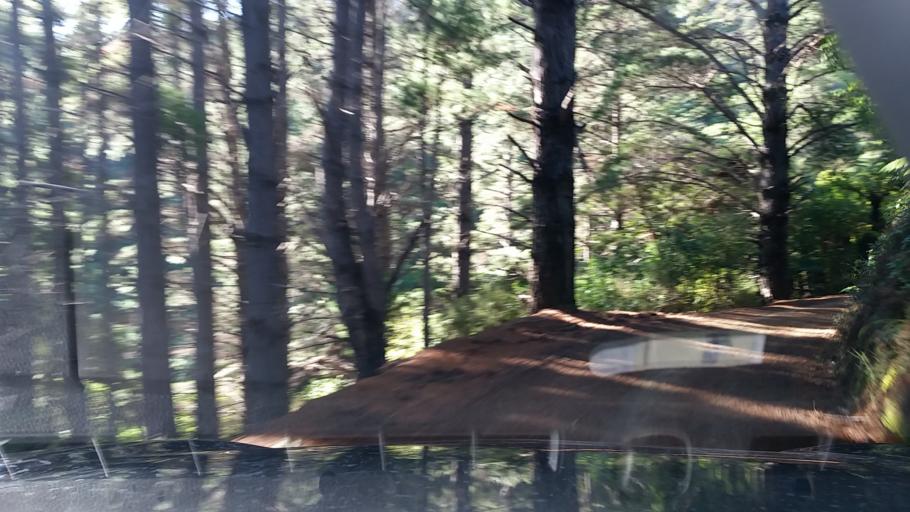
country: NZ
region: Marlborough
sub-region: Marlborough District
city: Picton
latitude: -41.1189
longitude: 173.9934
